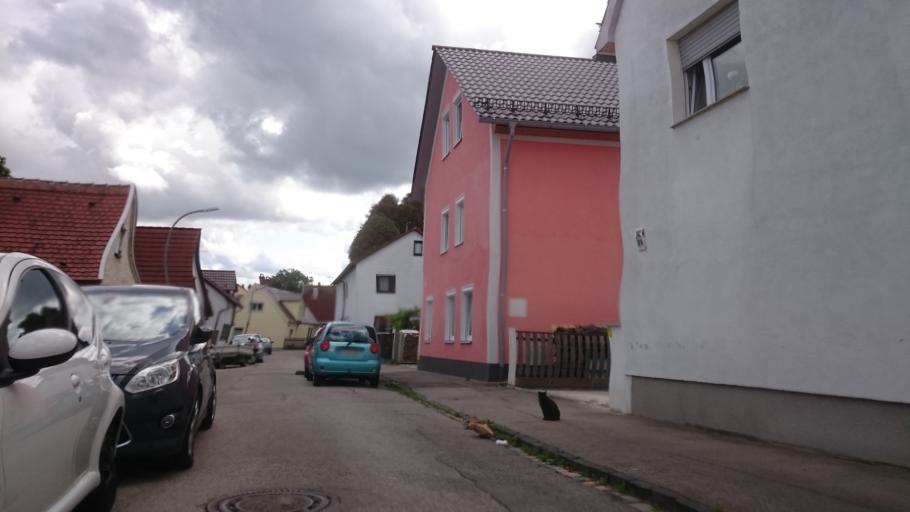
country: DE
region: Bavaria
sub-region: Swabia
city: Augsburg
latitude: 48.3769
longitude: 10.9209
